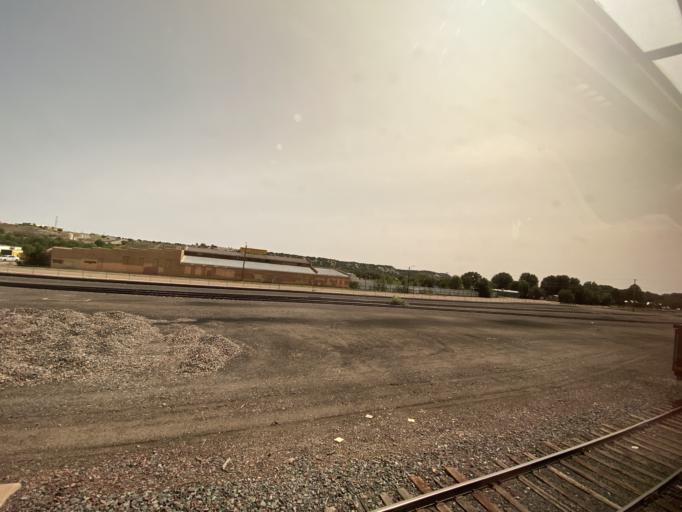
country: US
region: New Mexico
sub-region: San Miguel County
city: Las Vegas
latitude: 35.5931
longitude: -105.2124
